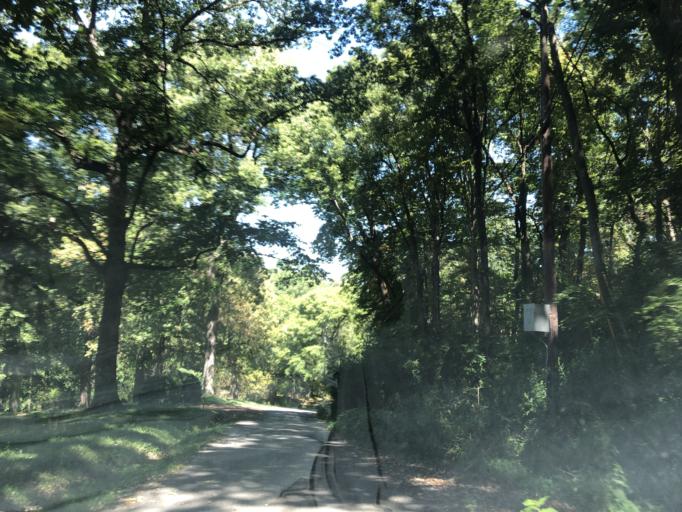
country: US
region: Tennessee
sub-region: Davidson County
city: Oak Hill
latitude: 36.0730
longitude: -86.7875
